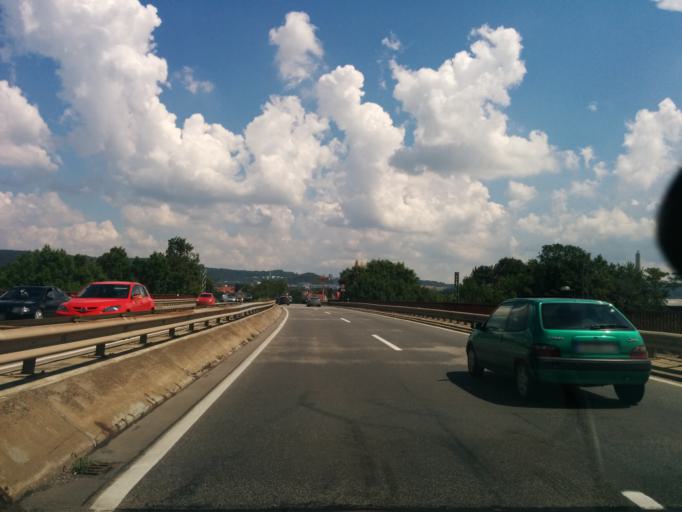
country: DE
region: Lower Saxony
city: Goettingen
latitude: 51.5561
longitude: 9.9227
